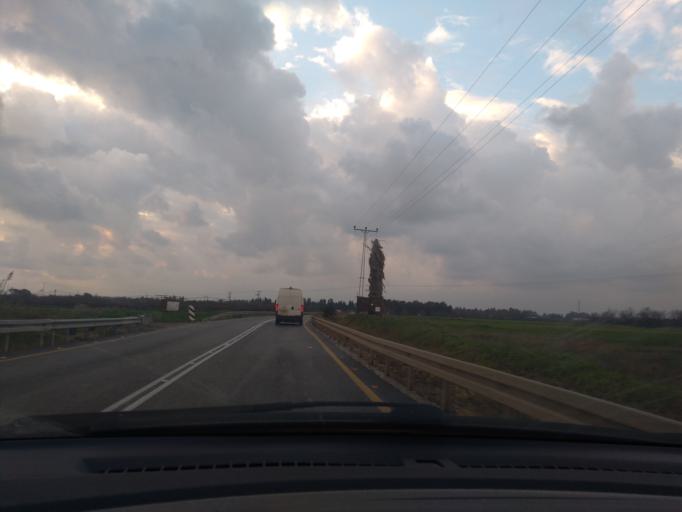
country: IL
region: Central District
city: Elyakhin
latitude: 32.3745
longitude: 34.9041
